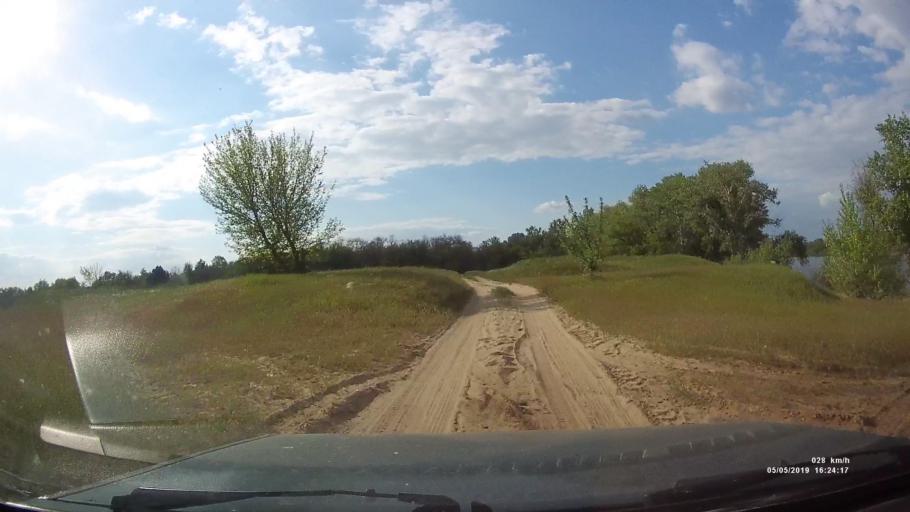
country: RU
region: Rostov
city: Konstantinovsk
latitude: 47.7589
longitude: 41.0268
